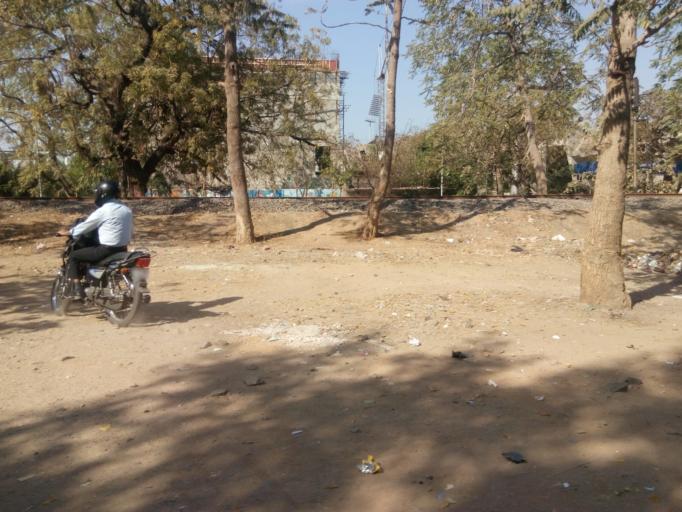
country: IN
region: Gujarat
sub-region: Ahmadabad
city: Ahmedabad
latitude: 23.0405
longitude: 72.5659
